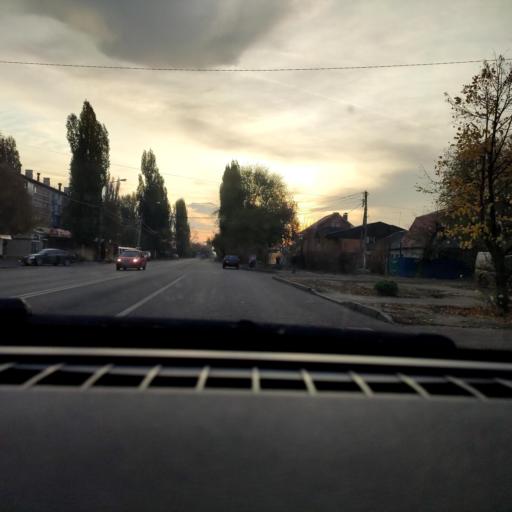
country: RU
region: Voronezj
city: Maslovka
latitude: 51.6331
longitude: 39.2675
